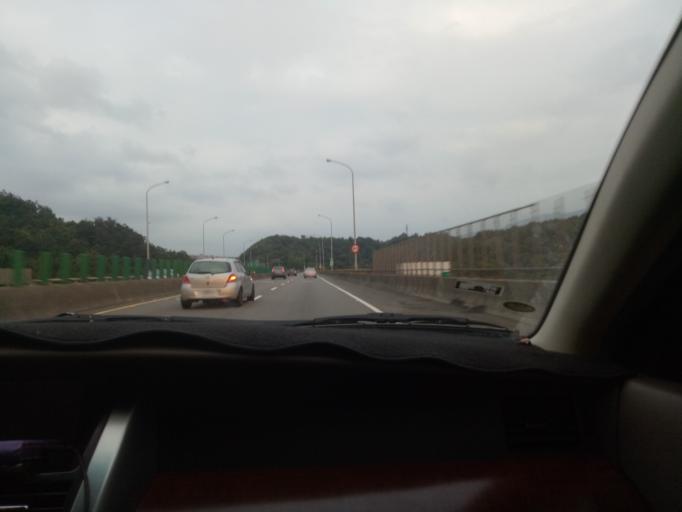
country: TW
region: Taiwan
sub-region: Keelung
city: Keelung
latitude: 25.1048
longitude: 121.7262
